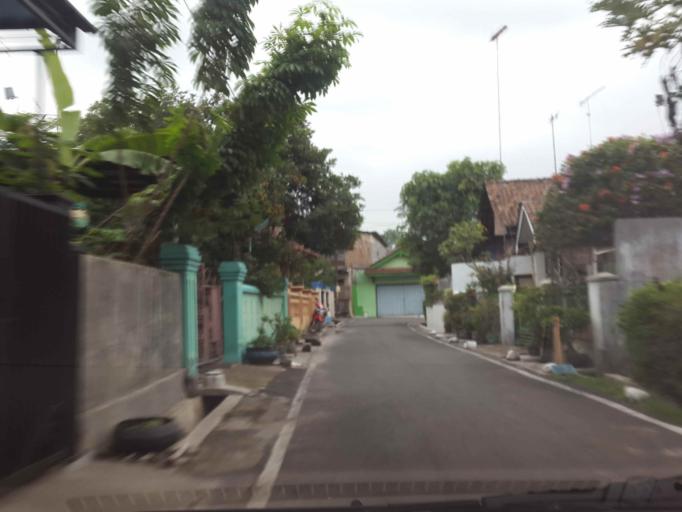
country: ID
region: Central Java
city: Salatiga
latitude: -7.3342
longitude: 110.4962
